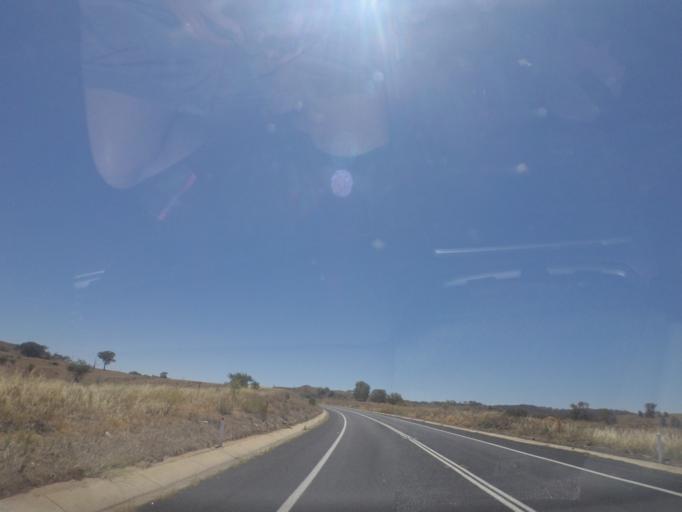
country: AU
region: New South Wales
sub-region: Warrumbungle Shire
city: Coonabarabran
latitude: -31.4261
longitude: 149.0975
